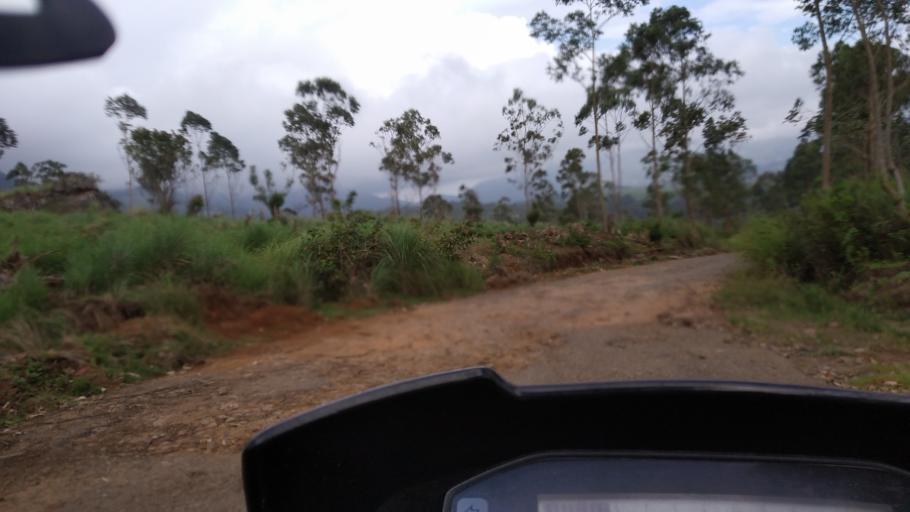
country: IN
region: Kerala
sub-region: Idukki
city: Munnar
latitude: 10.0373
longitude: 77.1874
